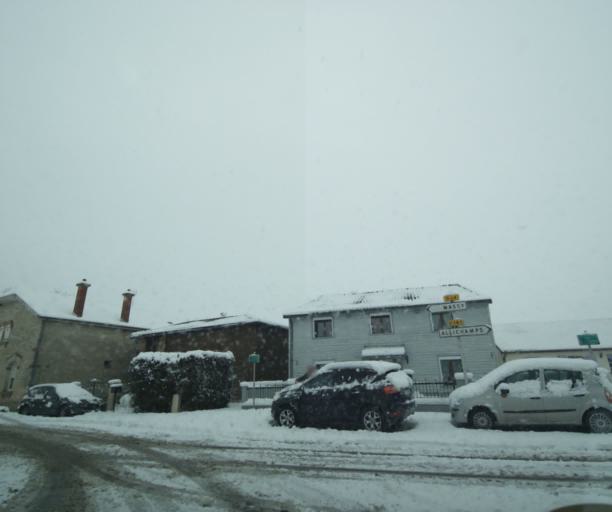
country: FR
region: Champagne-Ardenne
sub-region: Departement de la Haute-Marne
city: Saint-Dizier
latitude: 48.5814
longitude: 4.8975
